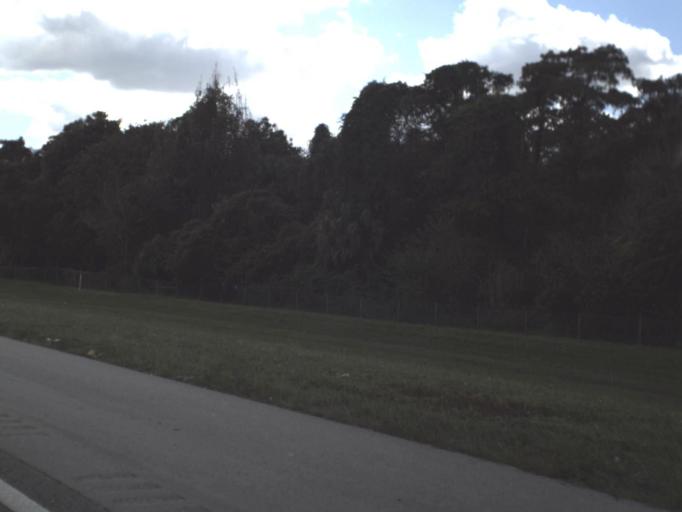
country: US
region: Florida
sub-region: Broward County
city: Coconut Creek
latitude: 26.2656
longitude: -80.1688
